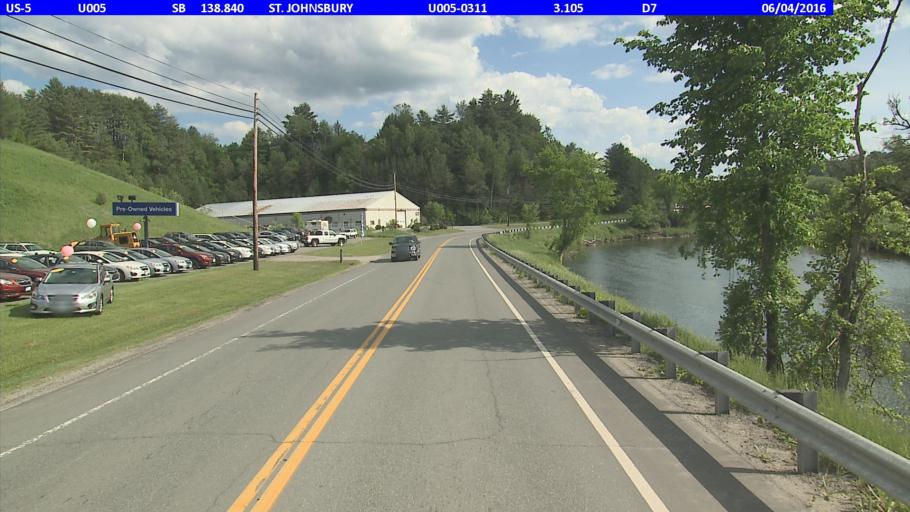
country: US
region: Vermont
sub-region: Caledonia County
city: St Johnsbury
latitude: 44.4367
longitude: -72.0161
